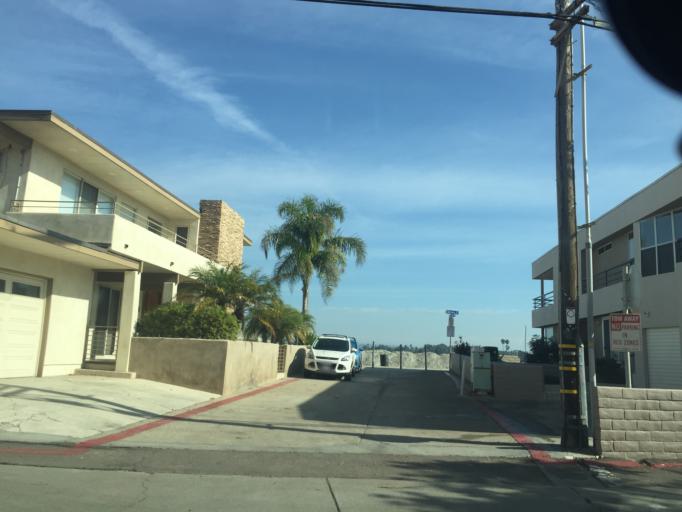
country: US
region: California
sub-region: San Diego County
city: La Jolla
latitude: 32.7762
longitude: -117.2518
